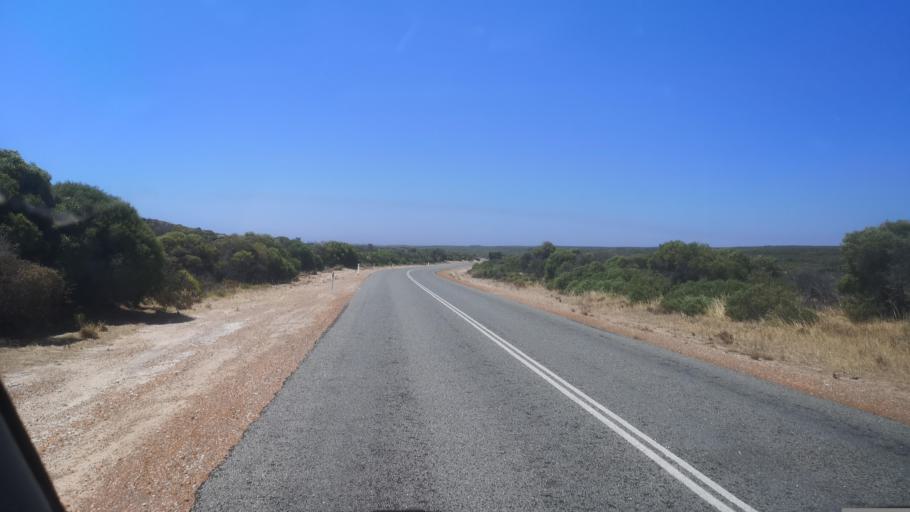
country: AU
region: Western Australia
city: Port Denison
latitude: -29.6572
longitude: 114.9655
